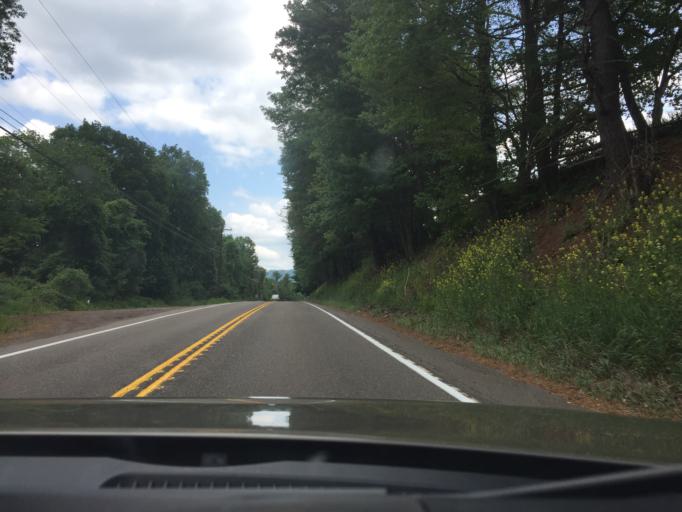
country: US
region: Pennsylvania
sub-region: Luzerne County
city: Conyngham
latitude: 41.0123
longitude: -76.0778
